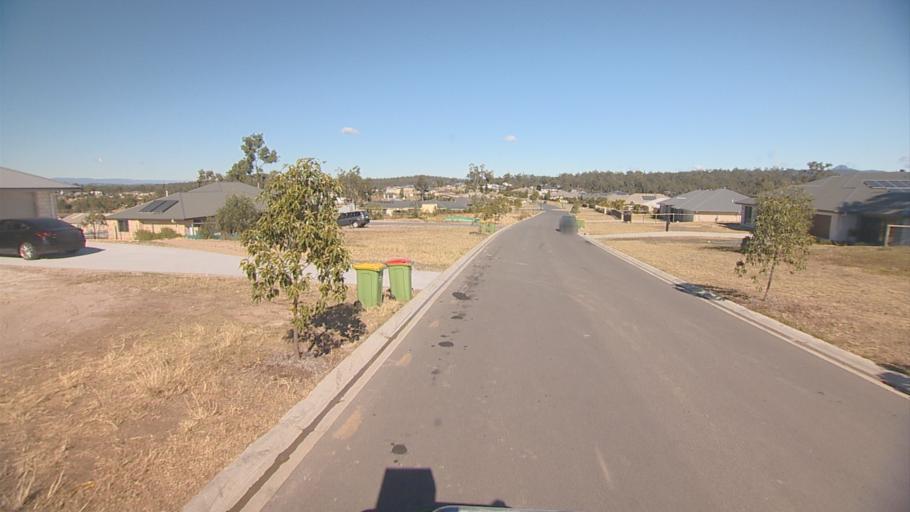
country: AU
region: Queensland
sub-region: Logan
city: North Maclean
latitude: -27.7503
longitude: 152.9466
